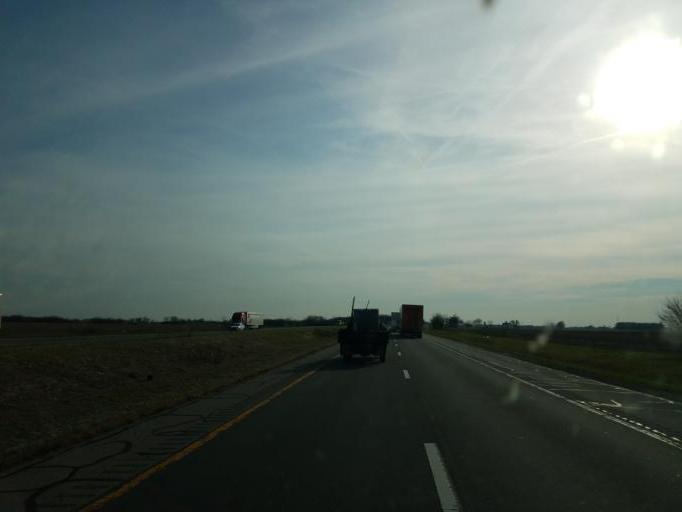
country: US
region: Ohio
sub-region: Madison County
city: Bethel
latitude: 39.7136
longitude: -83.4145
